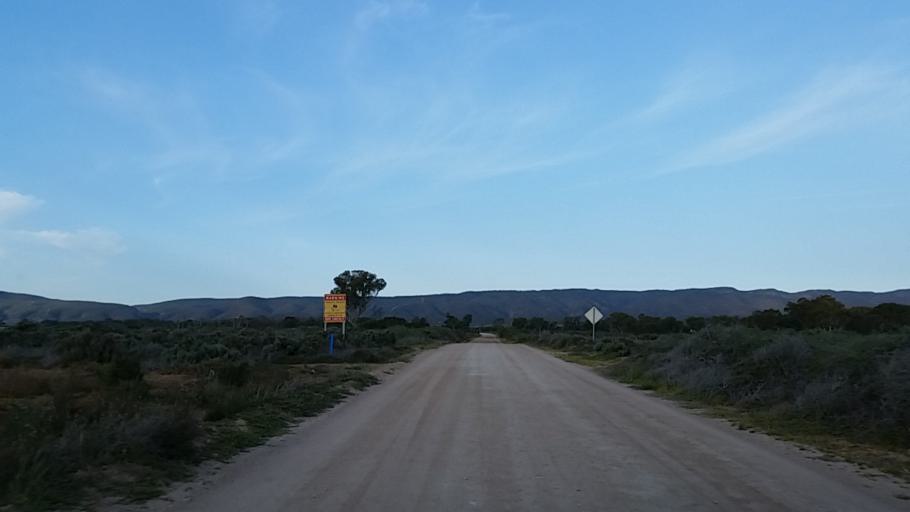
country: AU
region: South Australia
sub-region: Port Pirie City and Dists
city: Port Pirie
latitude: -33.0674
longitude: 138.0417
